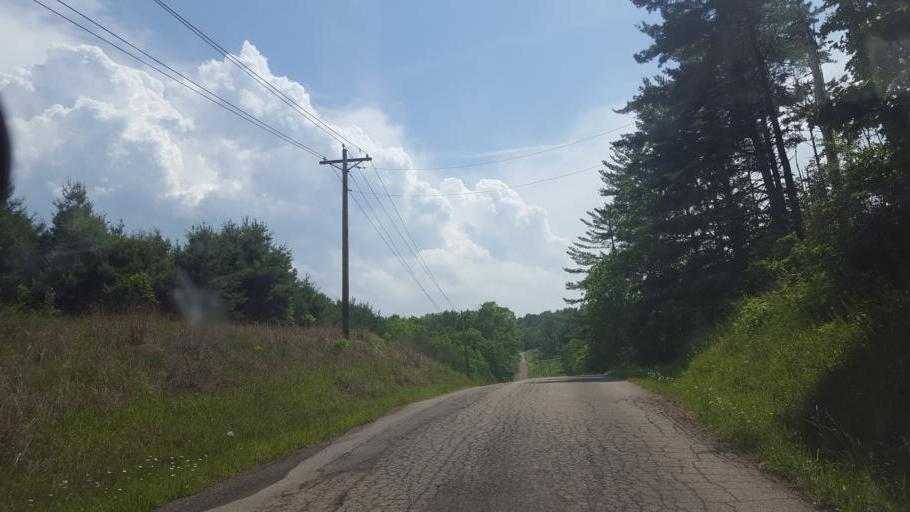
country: US
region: Ohio
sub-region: Knox County
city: Oak Hill
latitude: 40.3368
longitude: -82.2453
